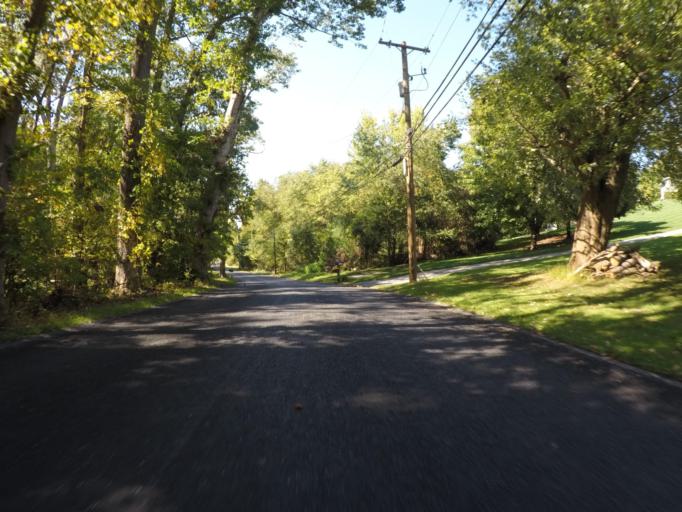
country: US
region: Maryland
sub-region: Carroll County
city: Hampstead
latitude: 39.5882
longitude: -76.8678
